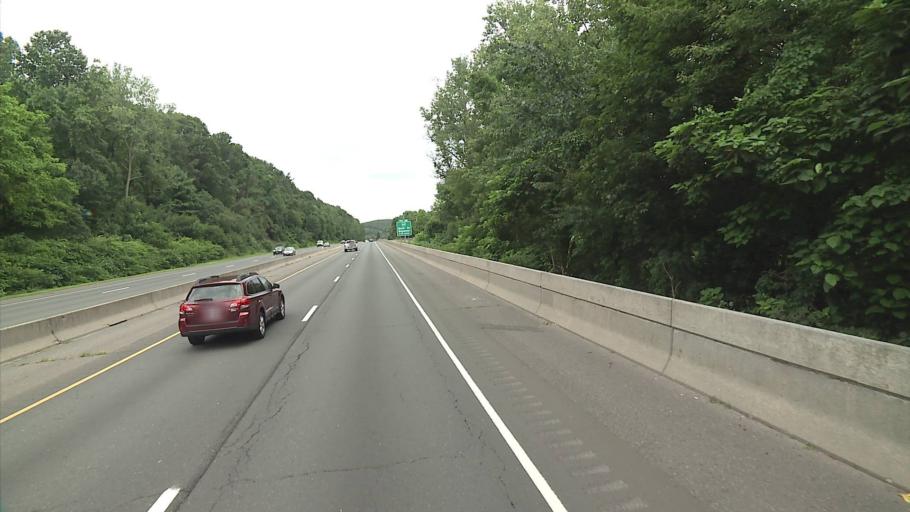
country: US
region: Connecticut
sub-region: New Haven County
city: Seymour
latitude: 41.4216
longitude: -73.0693
